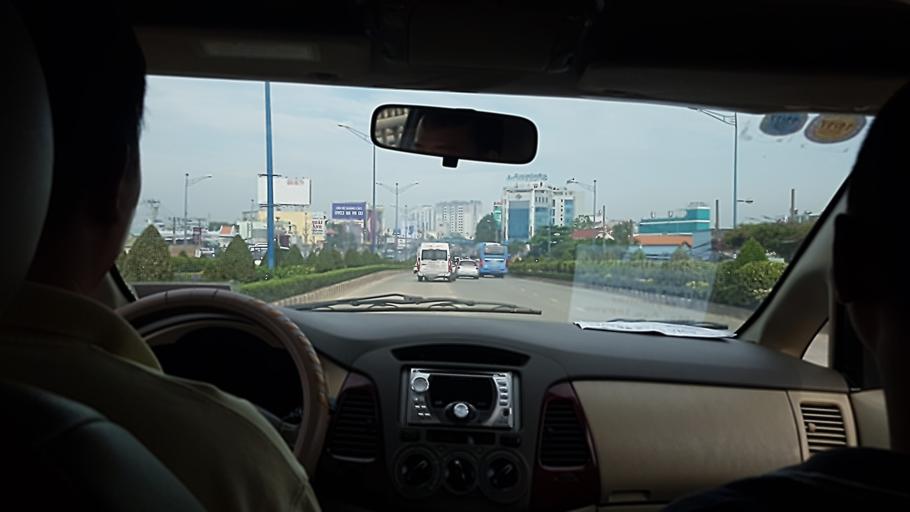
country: VN
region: Ho Chi Minh City
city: Ho Chi Minh City
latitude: 10.8249
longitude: 106.6278
